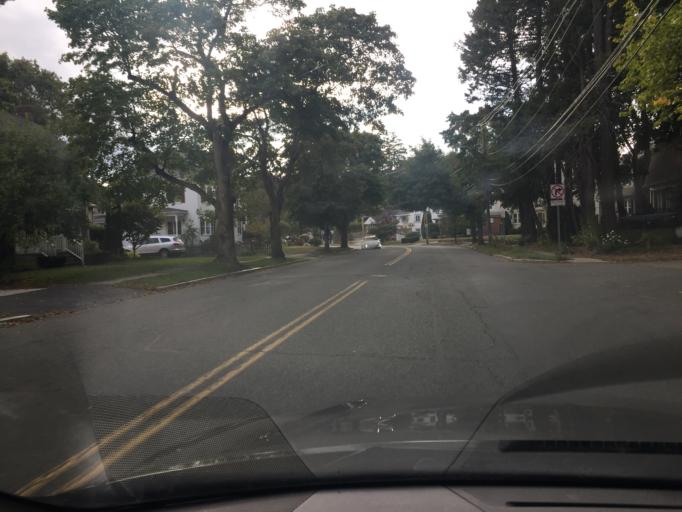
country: US
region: Massachusetts
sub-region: Middlesex County
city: Medford
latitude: 42.4246
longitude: -71.1196
